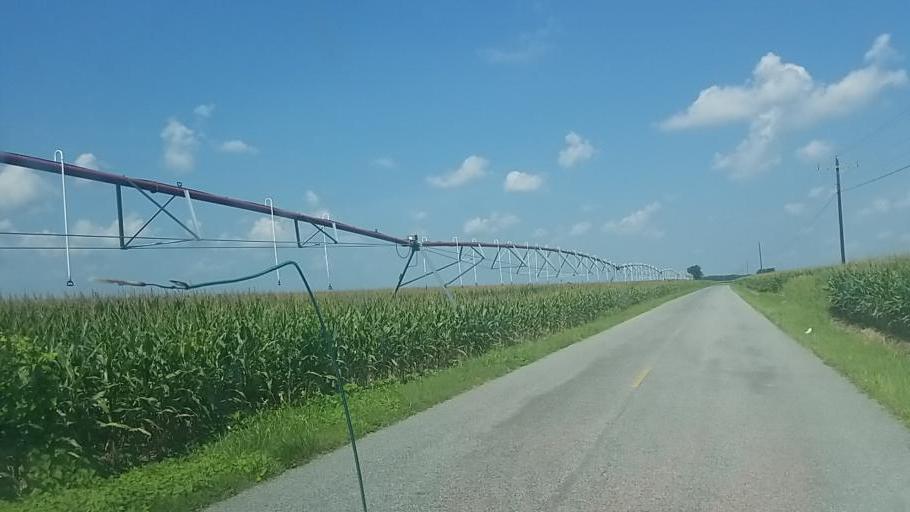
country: US
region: Maryland
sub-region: Worcester County
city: Berlin
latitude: 38.2896
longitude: -75.2420
